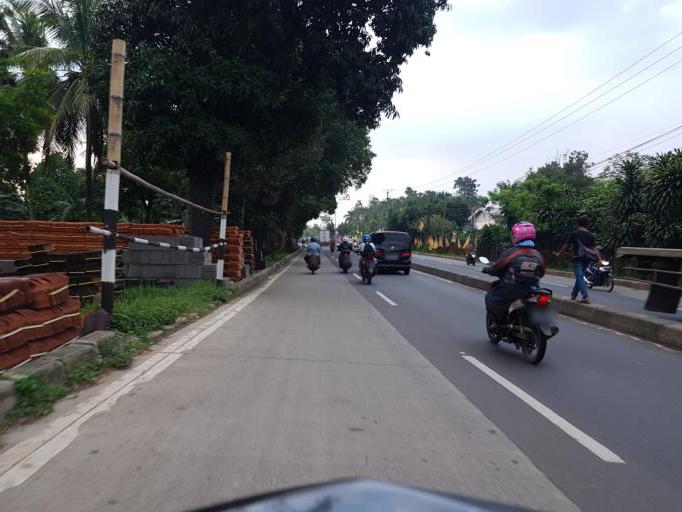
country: ID
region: West Java
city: Parung
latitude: -6.4940
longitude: 106.7473
